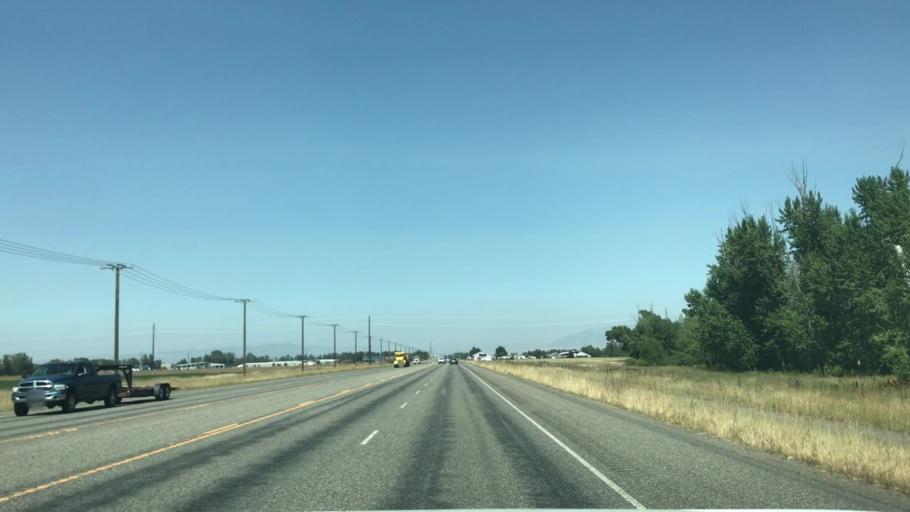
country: US
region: Montana
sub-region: Gallatin County
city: Four Corners
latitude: 45.6895
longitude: -111.1854
